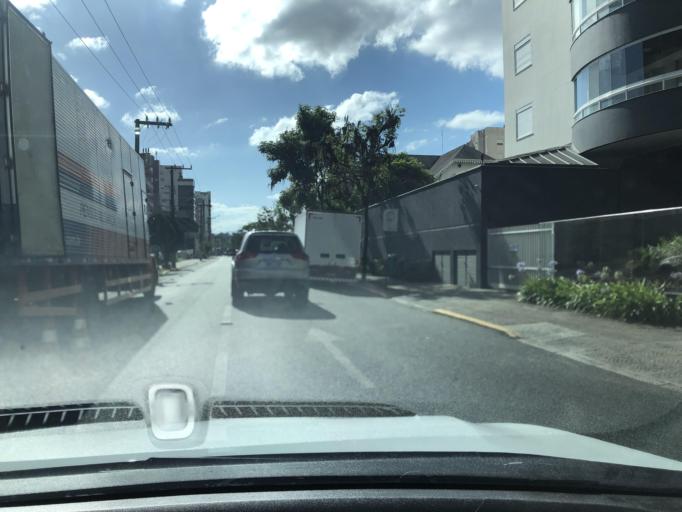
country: BR
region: Santa Catarina
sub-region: Joinville
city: Joinville
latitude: -26.2970
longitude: -48.8460
